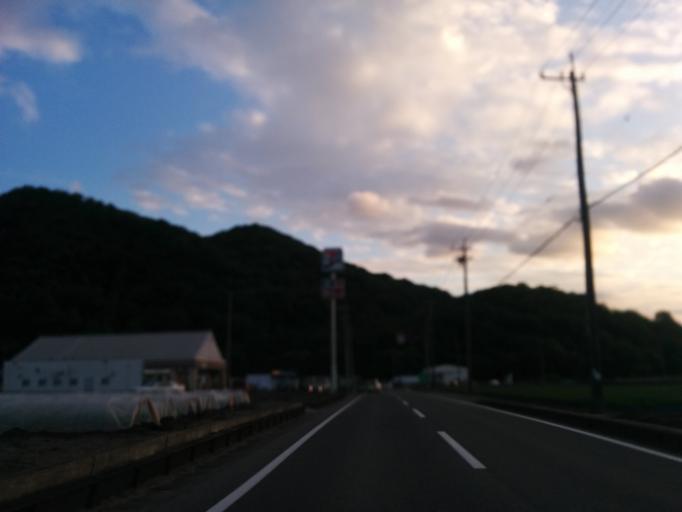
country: JP
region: Gifu
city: Inuyama
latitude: 35.3881
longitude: 136.9271
